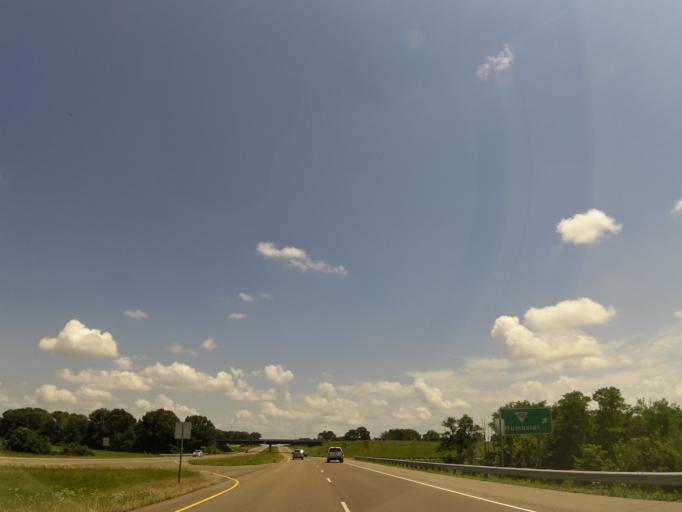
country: US
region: Tennessee
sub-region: Crockett County
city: Alamo
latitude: 35.8384
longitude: -89.1878
